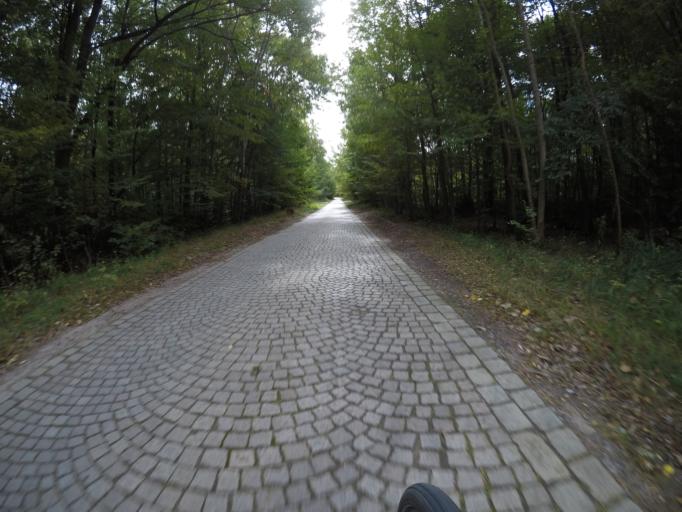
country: DE
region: Baden-Wuerttemberg
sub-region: Regierungsbezirk Stuttgart
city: Schonaich
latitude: 48.6754
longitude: 9.0511
